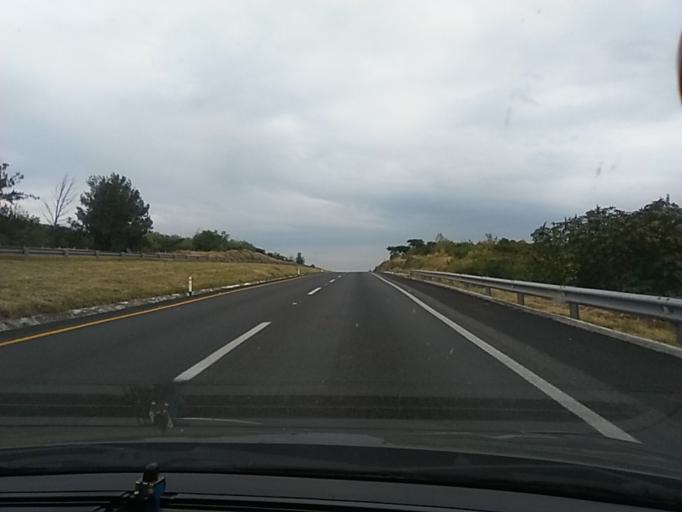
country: MX
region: Michoacan
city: Churintzio
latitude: 20.1133
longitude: -102.0443
